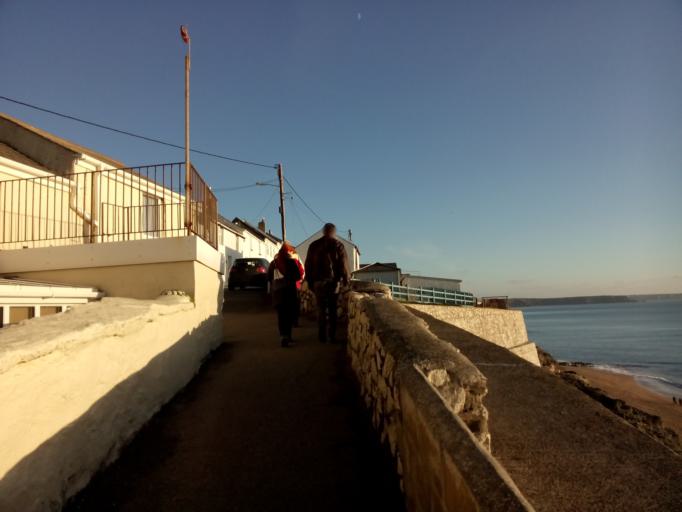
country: GB
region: England
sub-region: Cornwall
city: Porthleven
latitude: 50.0806
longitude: -5.3124
